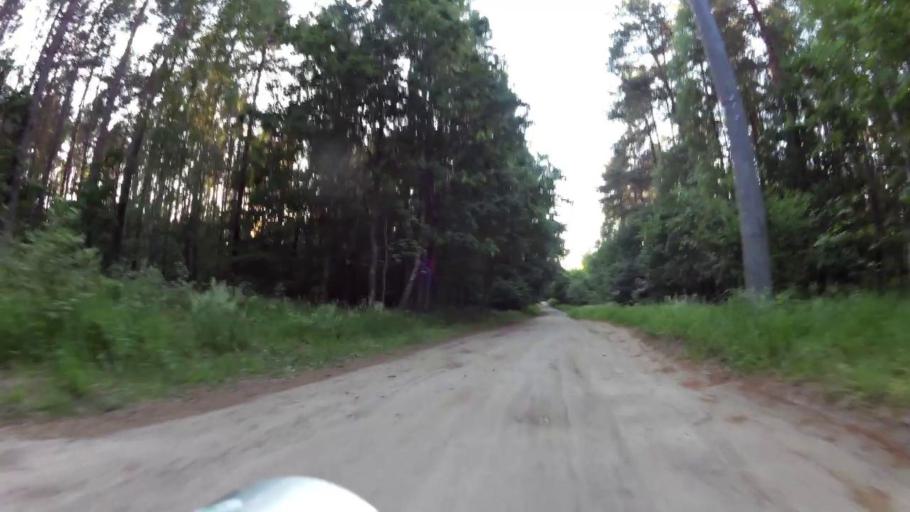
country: PL
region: West Pomeranian Voivodeship
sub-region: Powiat szczecinecki
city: Szczecinek
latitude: 53.8273
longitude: 16.6898
